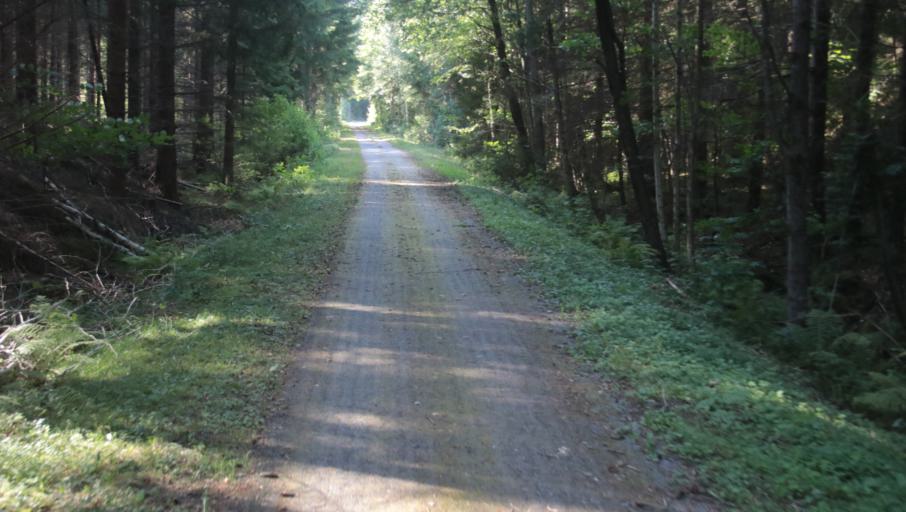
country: SE
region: Blekinge
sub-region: Karlshamns Kommun
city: Svangsta
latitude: 56.3080
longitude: 14.7227
